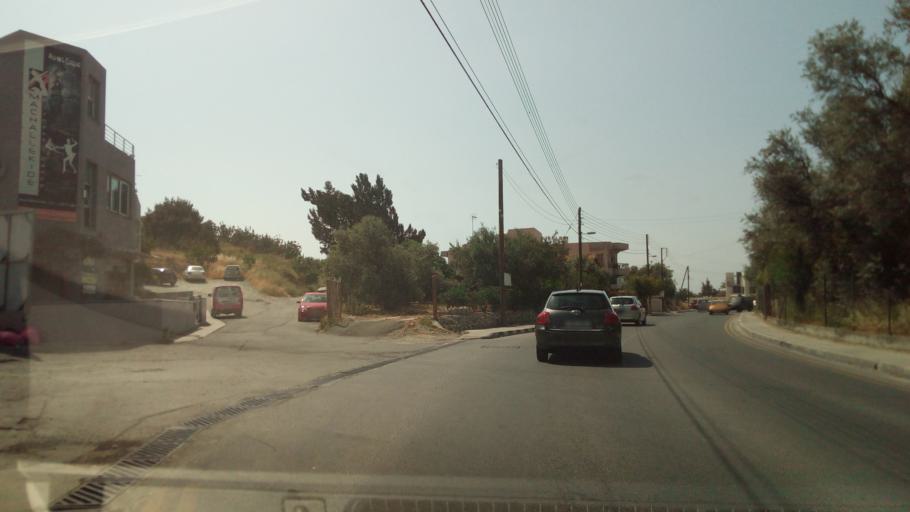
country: CY
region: Limassol
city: Limassol
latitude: 34.7098
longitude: 33.0244
